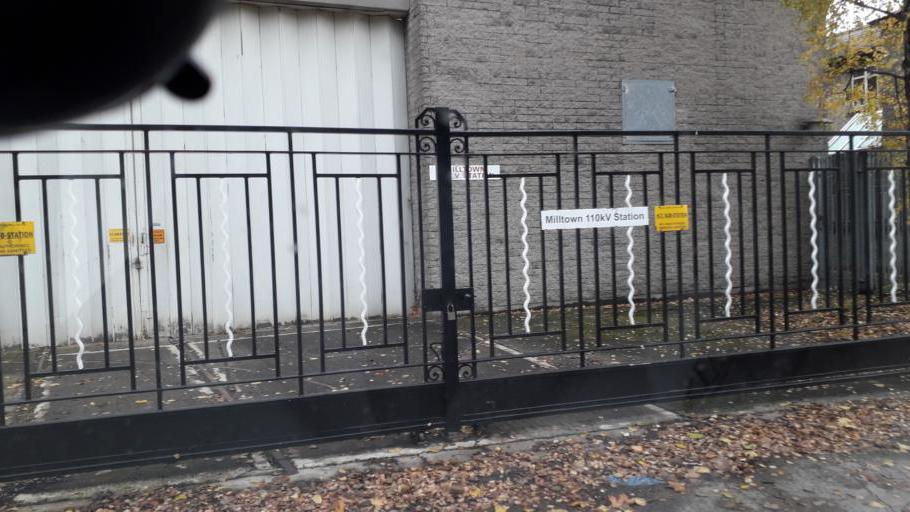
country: IE
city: Milltown
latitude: 53.3151
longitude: -6.2514
